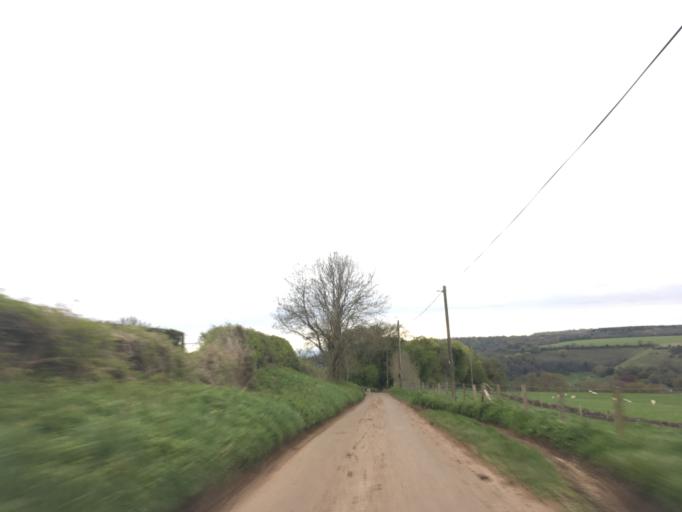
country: GB
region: England
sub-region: Gloucestershire
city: Wotton-under-Edge
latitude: 51.6393
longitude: -2.3283
